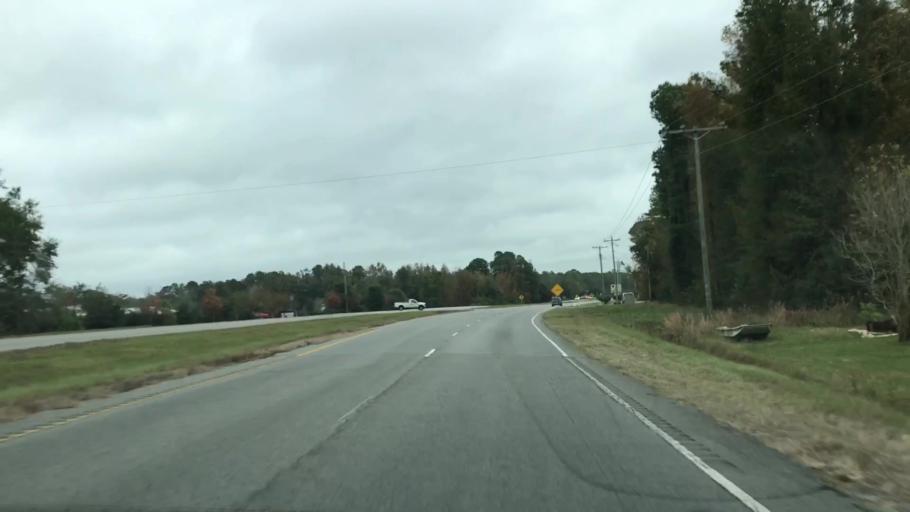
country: US
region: South Carolina
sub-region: Charleston County
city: Awendaw
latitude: 33.0264
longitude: -79.6285
